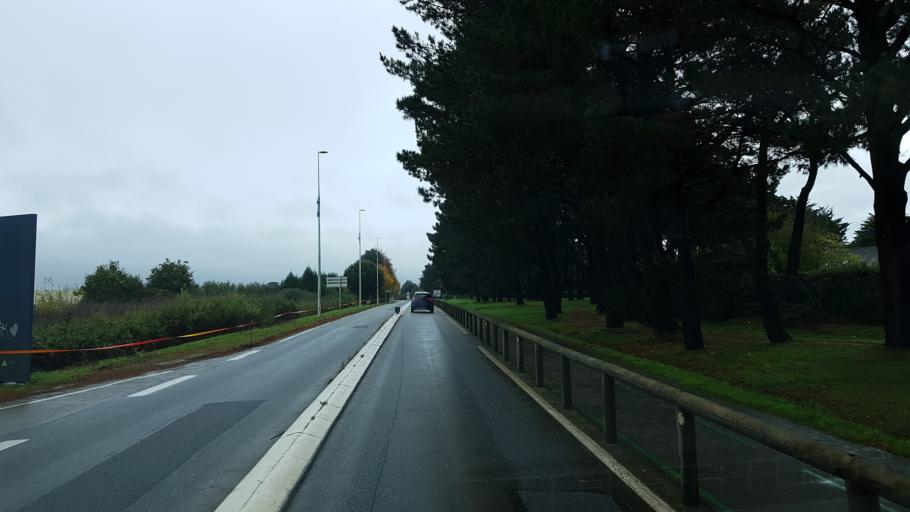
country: FR
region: Brittany
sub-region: Departement du Morbihan
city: Arzon
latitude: 47.5432
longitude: -2.8832
